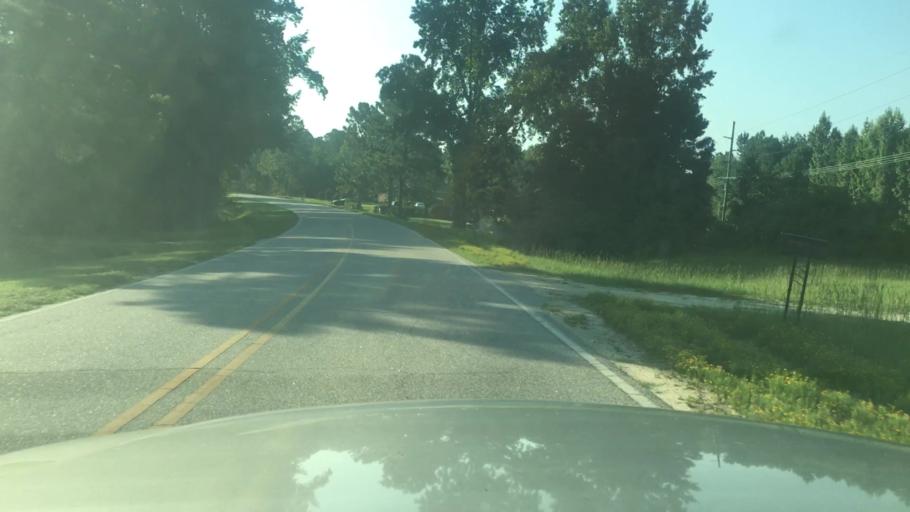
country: US
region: North Carolina
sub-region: Cumberland County
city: Spring Lake
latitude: 35.2078
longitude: -78.8927
